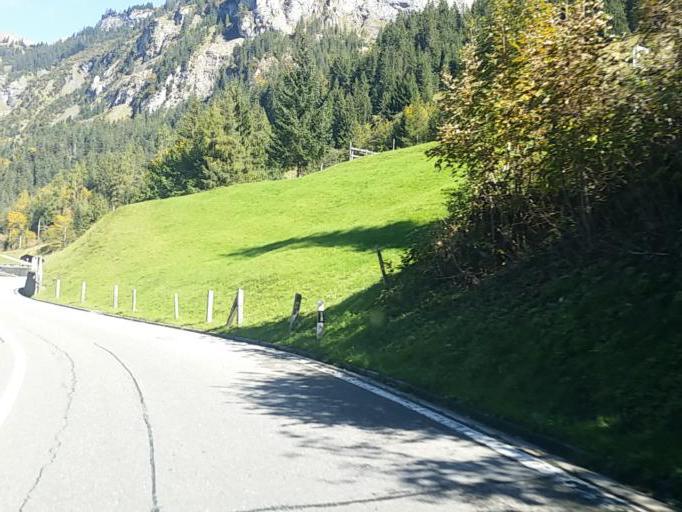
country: CH
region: Bern
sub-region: Frutigen-Niedersimmental District
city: Kandersteg
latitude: 46.5109
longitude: 7.6759
